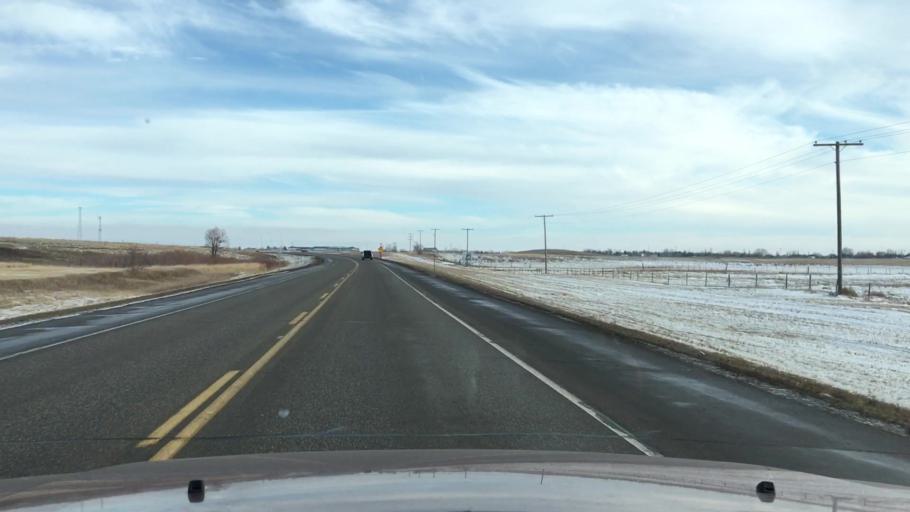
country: CA
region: Saskatchewan
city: Pilot Butte
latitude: 50.4844
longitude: -104.4452
